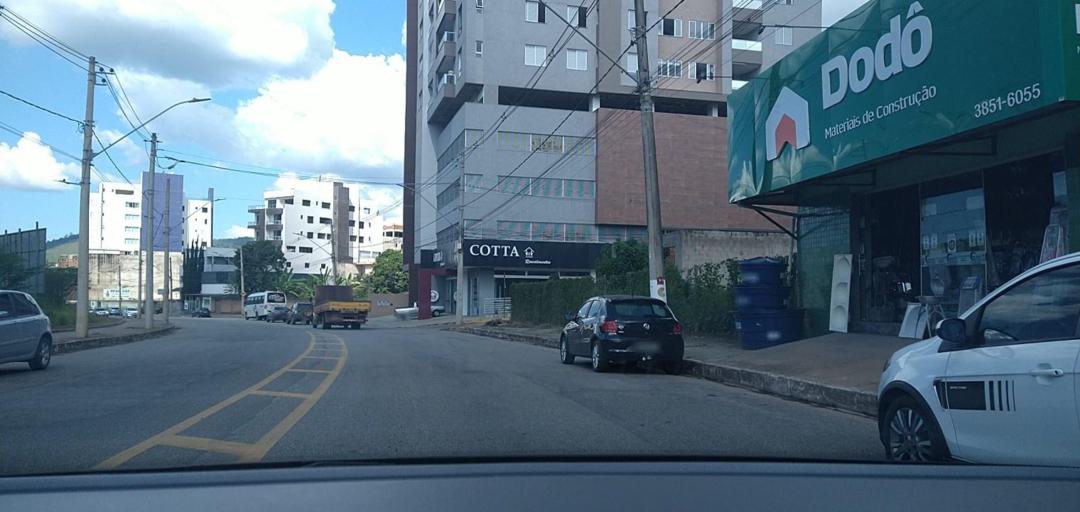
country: BR
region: Minas Gerais
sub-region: Joao Monlevade
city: Joao Monlevade
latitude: -19.8113
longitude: -43.1906
